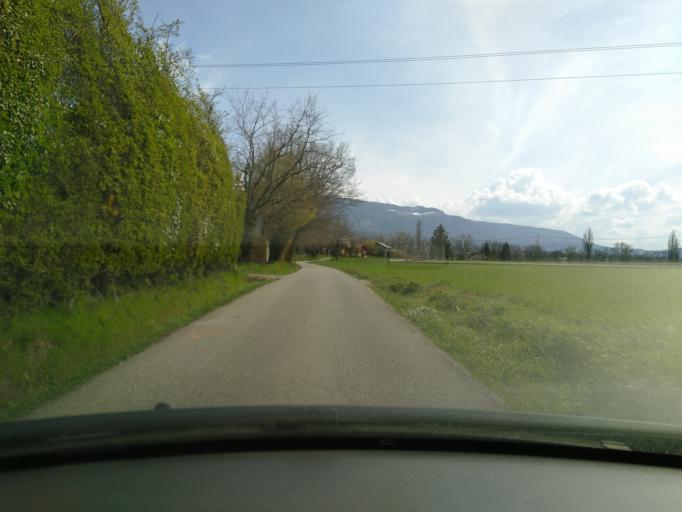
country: FR
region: Rhone-Alpes
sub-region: Departement de la Haute-Savoie
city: Neydens
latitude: 46.1404
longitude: 6.1072
